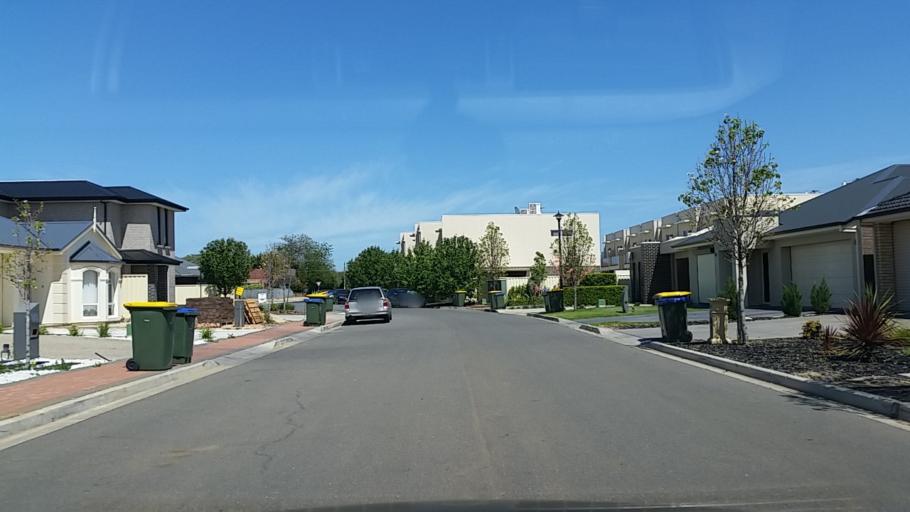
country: AU
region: South Australia
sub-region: Charles Sturt
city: Findon
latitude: -34.9023
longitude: 138.5289
